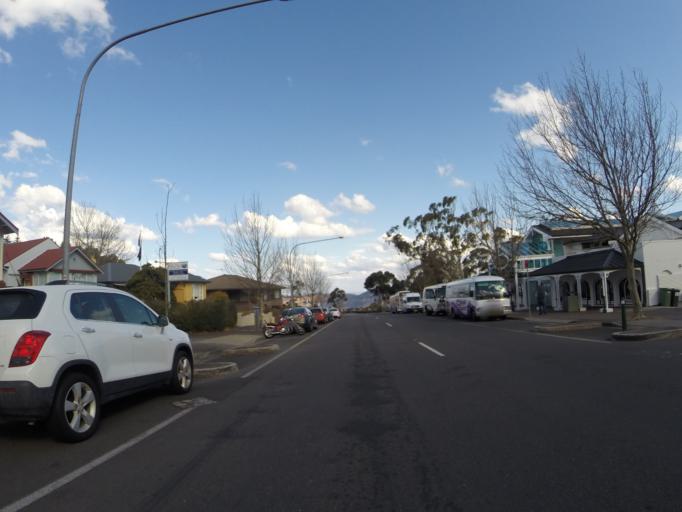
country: AU
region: New South Wales
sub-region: Blue Mountains Municipality
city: Katoomba
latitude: -33.7307
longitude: 150.3119
